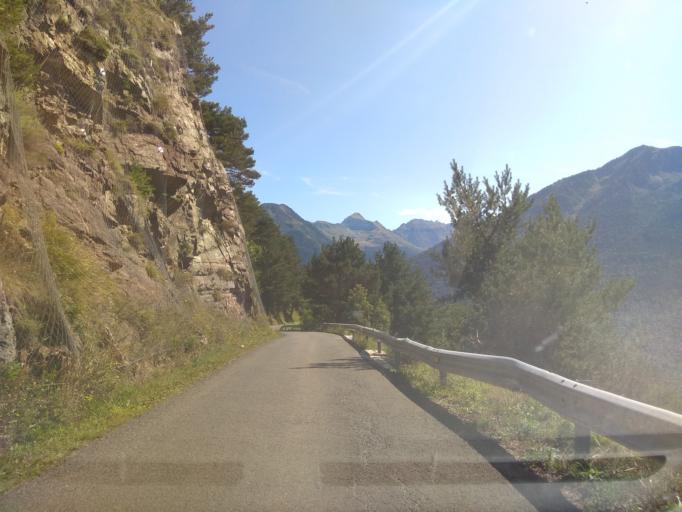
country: ES
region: Catalonia
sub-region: Provincia de Lleida
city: Les
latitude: 42.7544
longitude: 0.7143
